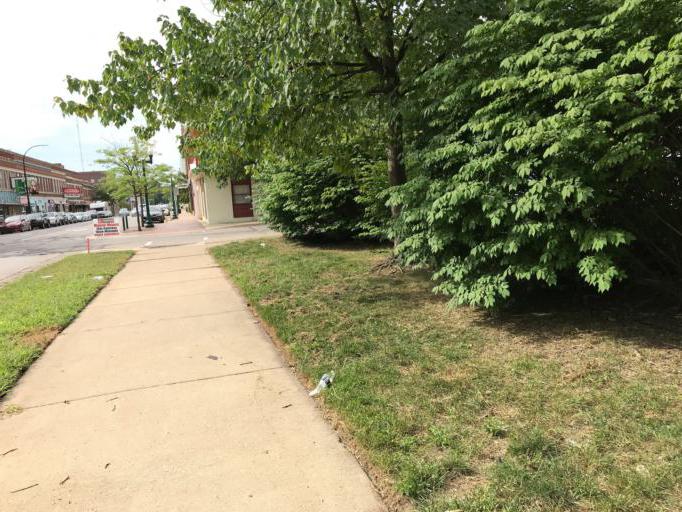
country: US
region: Michigan
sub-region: Washtenaw County
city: Ypsilanti
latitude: 42.2425
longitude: -83.6132
